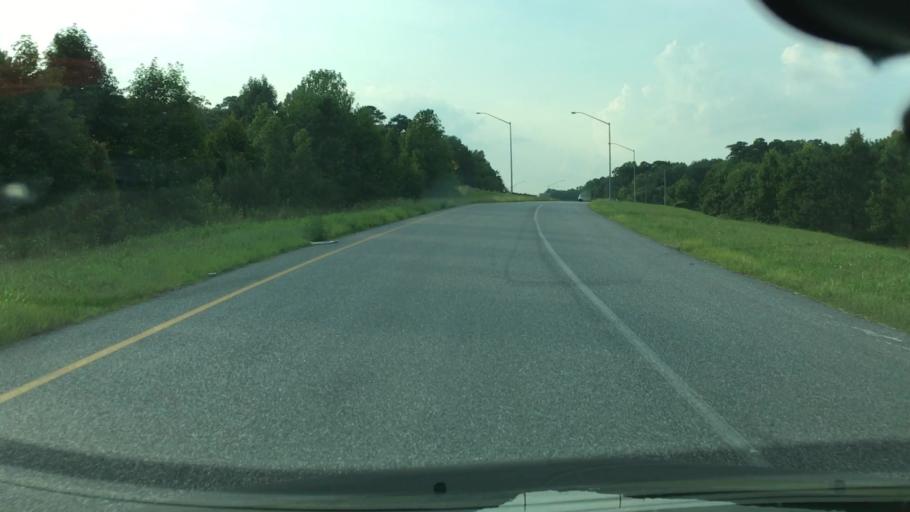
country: US
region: Maryland
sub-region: Worcester County
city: Ocean Pines
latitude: 38.3914
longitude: -75.2029
